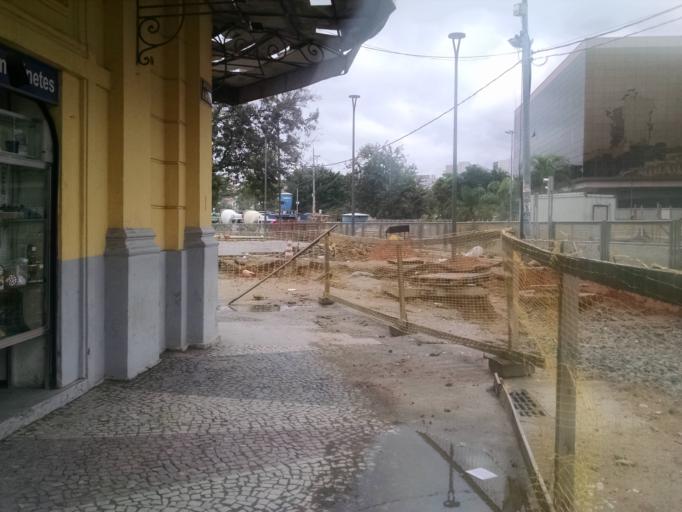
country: BR
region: Rio de Janeiro
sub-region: Rio De Janeiro
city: Rio de Janeiro
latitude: -22.9039
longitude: -43.1721
